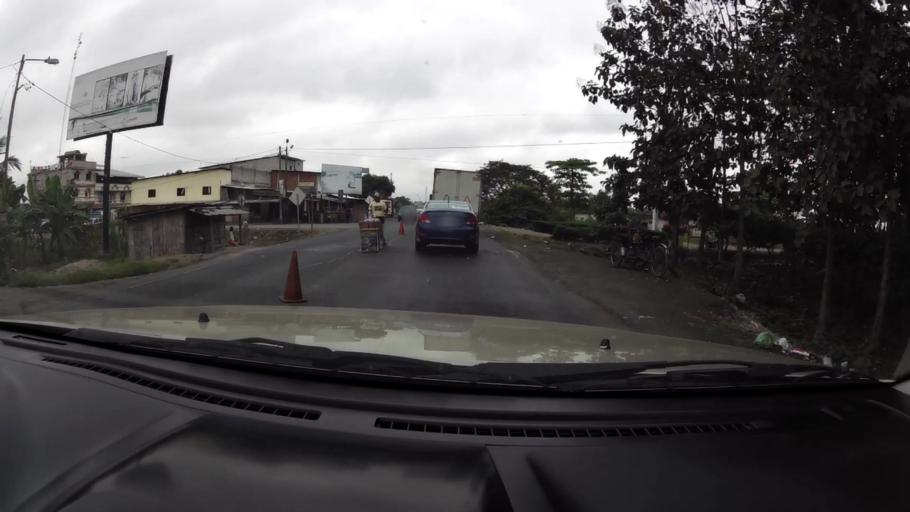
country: EC
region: Guayas
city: Naranjal
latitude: -2.7987
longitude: -79.7078
